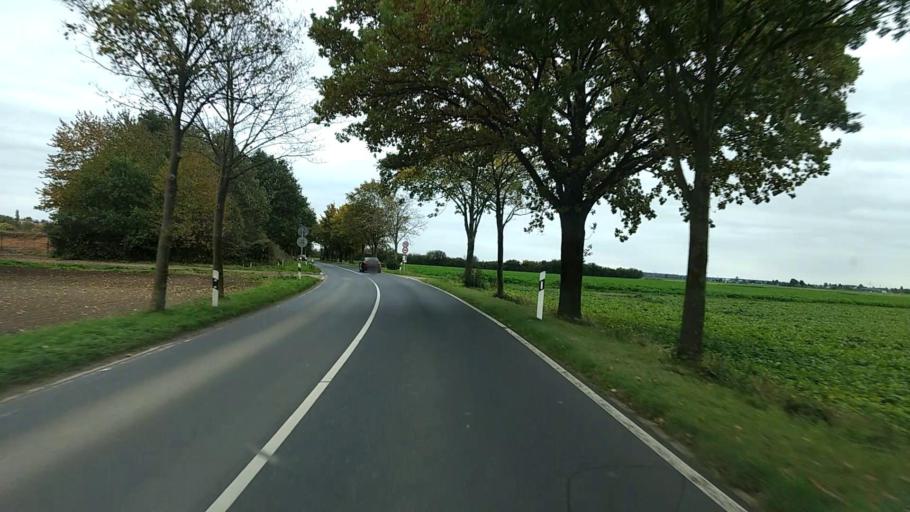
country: DE
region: North Rhine-Westphalia
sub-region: Regierungsbezirk Koln
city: Bergheim
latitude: 50.9293
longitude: 6.6432
